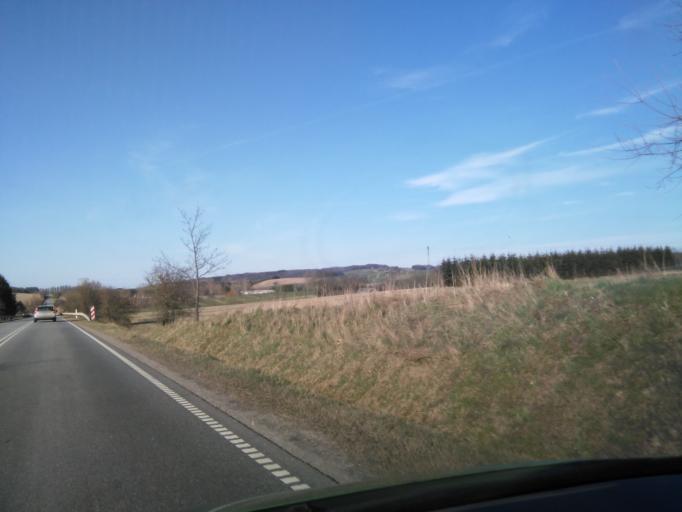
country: DK
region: Central Jutland
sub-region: Skanderborg Kommune
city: Ry
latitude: 55.9754
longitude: 9.7577
